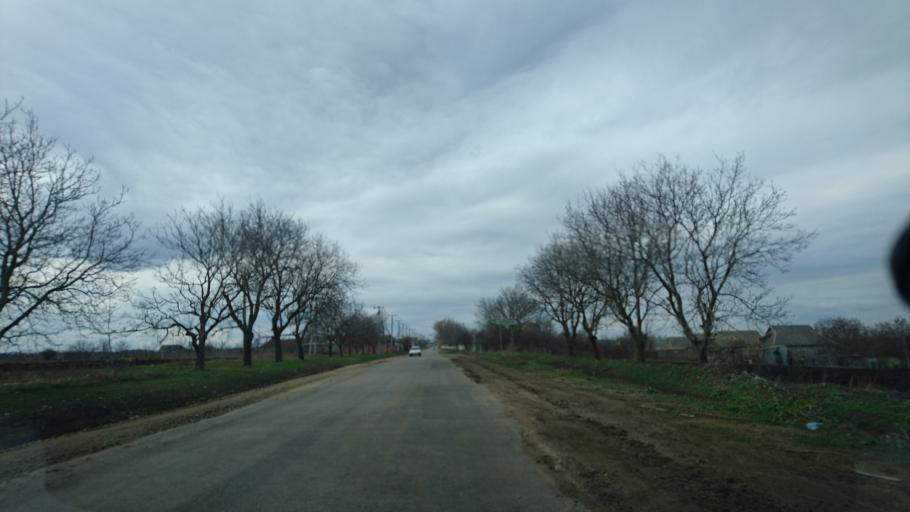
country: MD
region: Cantemir
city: Visniovca
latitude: 46.3477
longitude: 28.4177
